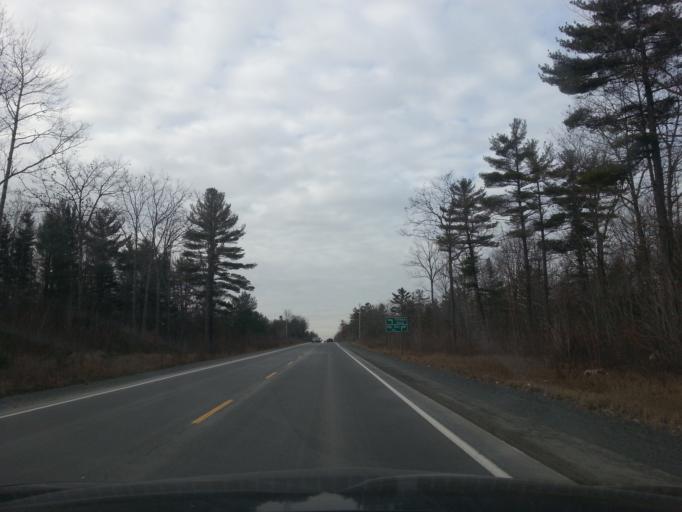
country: CA
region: Ontario
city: Quinte West
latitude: 44.4683
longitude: -77.7179
